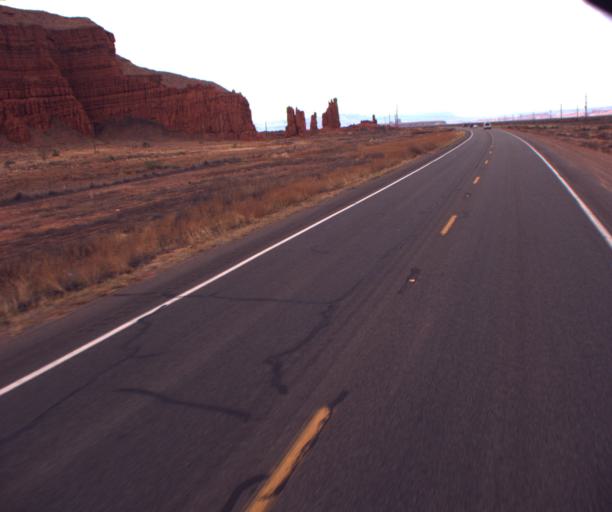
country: US
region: Arizona
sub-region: Navajo County
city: Kayenta
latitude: 36.7767
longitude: -110.0121
